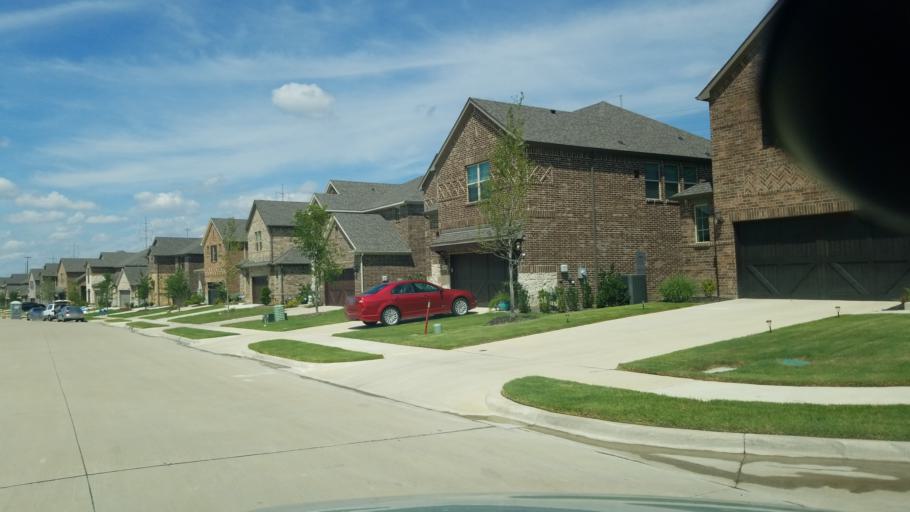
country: US
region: Texas
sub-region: Dallas County
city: Irving
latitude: 32.8512
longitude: -96.9294
